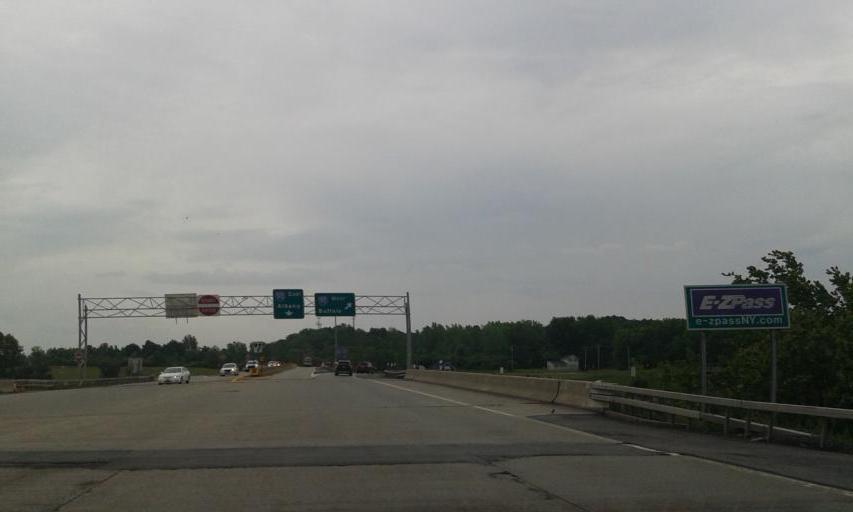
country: US
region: New York
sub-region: Onondaga County
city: Seneca Knolls
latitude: 43.1094
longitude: -76.2887
